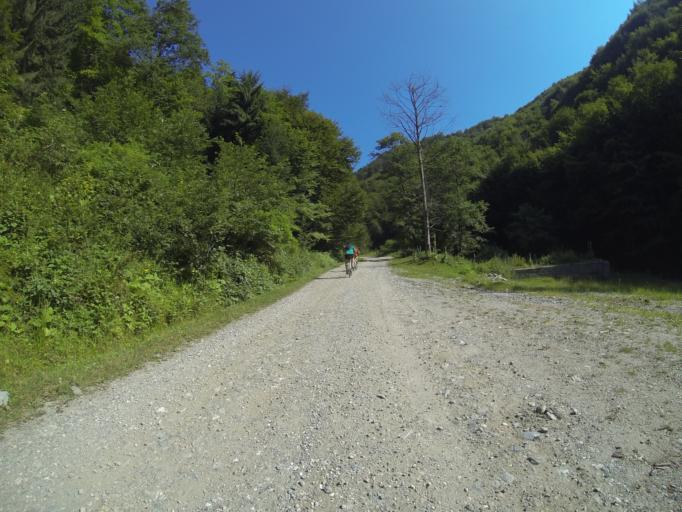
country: RO
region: Valcea
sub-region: Comuna Costesti
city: Bistrita
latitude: 45.2335
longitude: 24.0024
